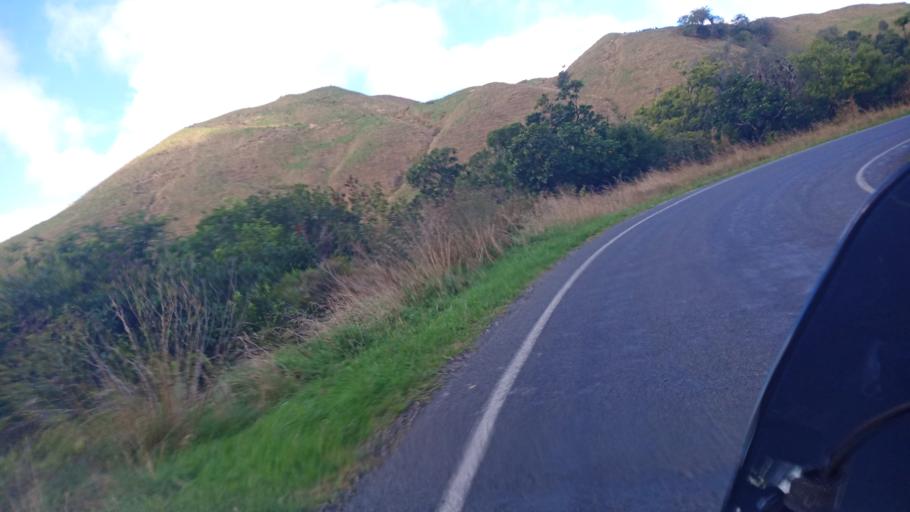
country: NZ
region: Gisborne
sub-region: Gisborne District
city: Gisborne
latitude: -38.5301
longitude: 177.5447
